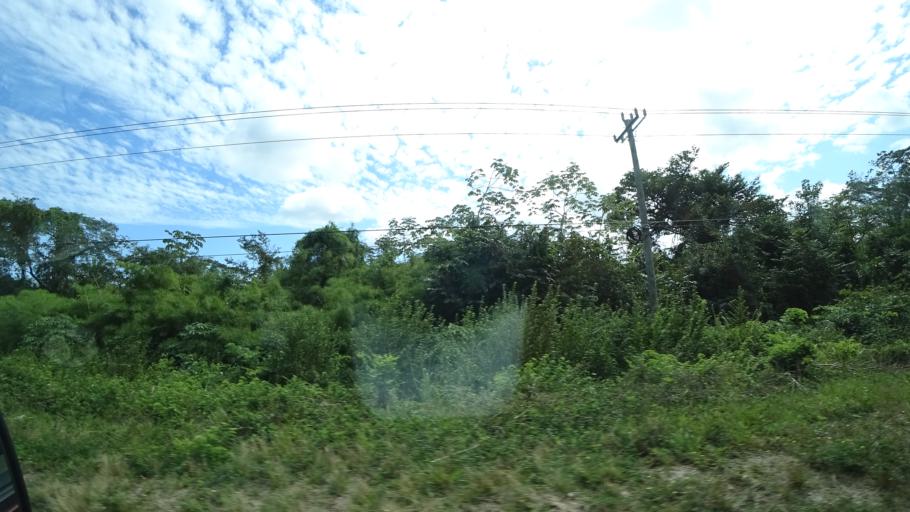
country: BZ
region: Belize
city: Belize City
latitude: 17.5680
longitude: -88.3898
